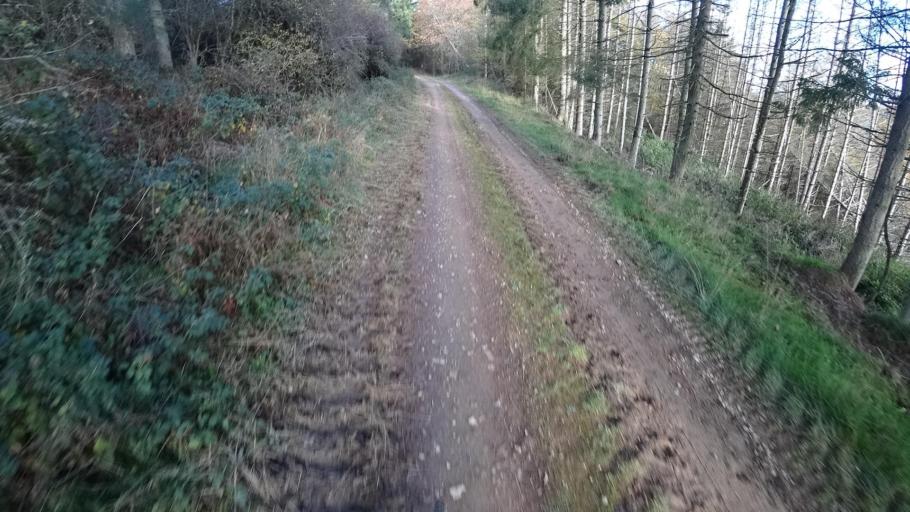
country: DE
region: Rheinland-Pfalz
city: Honningen
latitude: 50.4749
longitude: 6.9405
